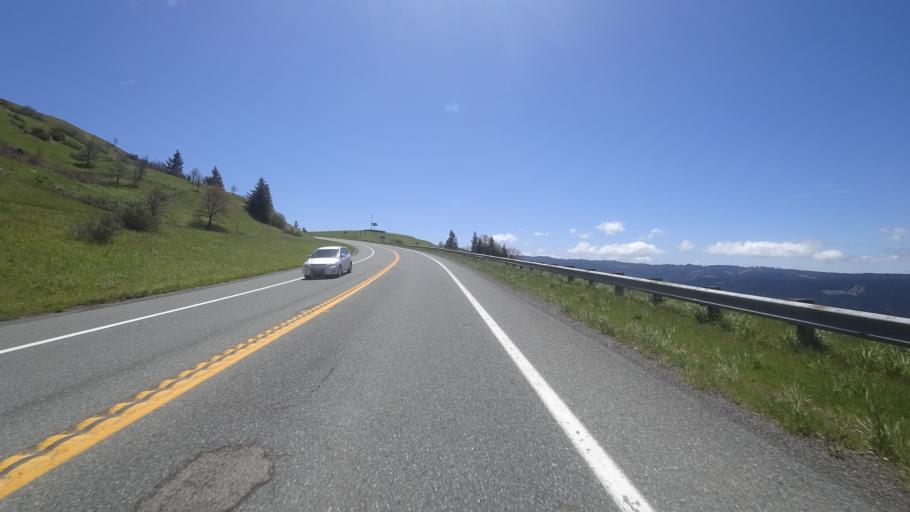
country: US
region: California
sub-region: Humboldt County
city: Willow Creek
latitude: 40.9040
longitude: -123.7812
